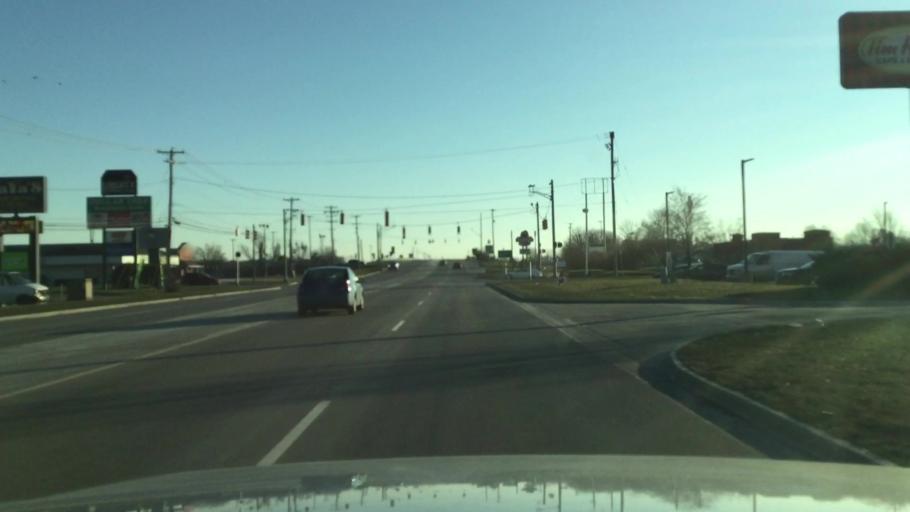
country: US
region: Michigan
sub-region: Genesee County
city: Beecher
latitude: 43.0605
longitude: -83.7675
